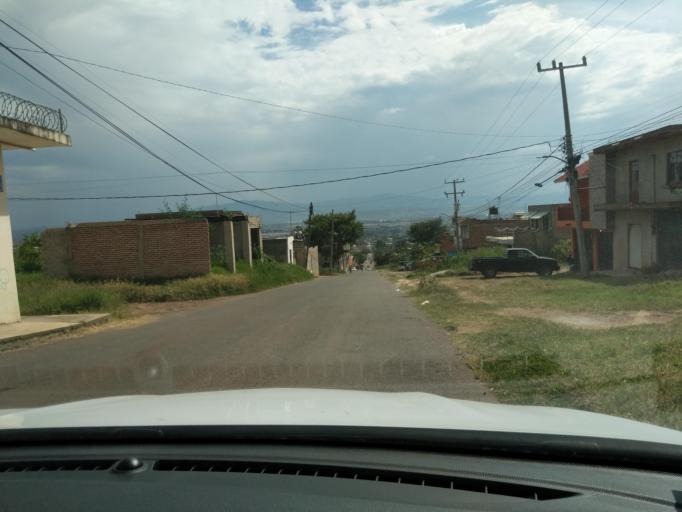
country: MX
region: Jalisco
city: San Jose del Castillo
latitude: 20.5224
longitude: -103.2339
